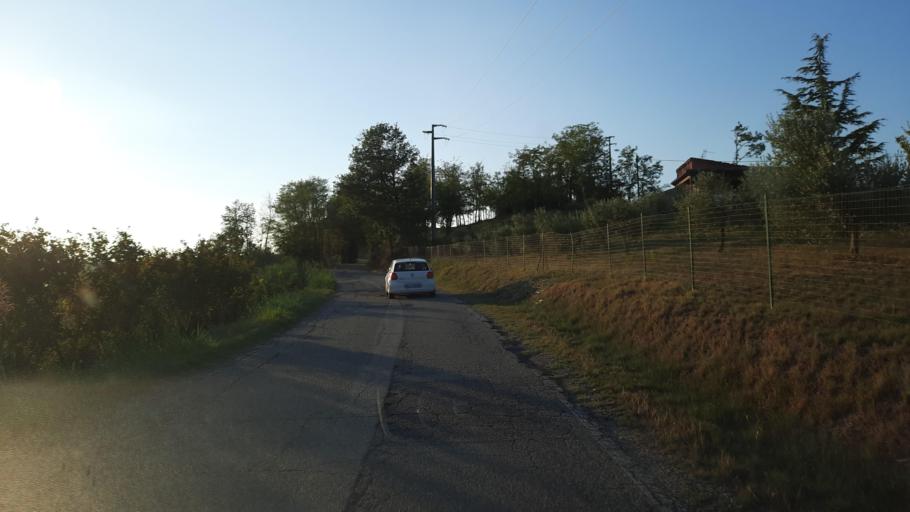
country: IT
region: Piedmont
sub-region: Provincia di Alessandria
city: Cereseto
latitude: 45.0770
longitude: 8.3238
